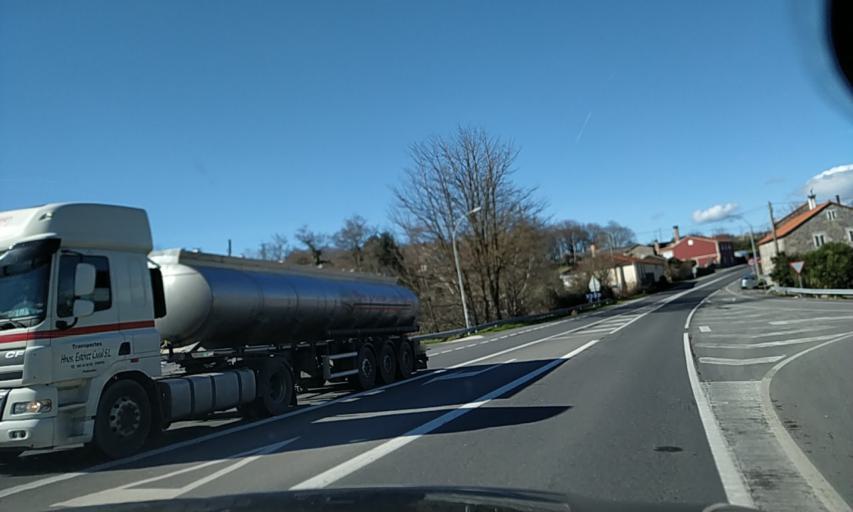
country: ES
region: Galicia
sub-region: Provincia de Pontevedra
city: Lalin
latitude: 42.6749
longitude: -8.1638
